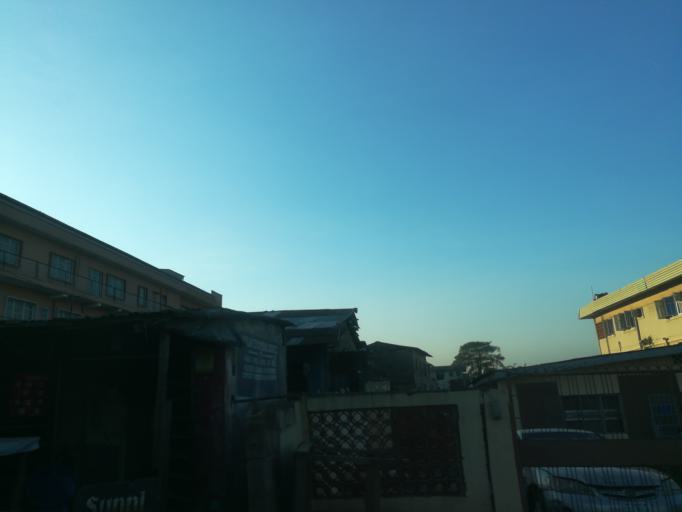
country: NG
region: Lagos
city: Ikorodu
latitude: 6.6151
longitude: 3.5122
